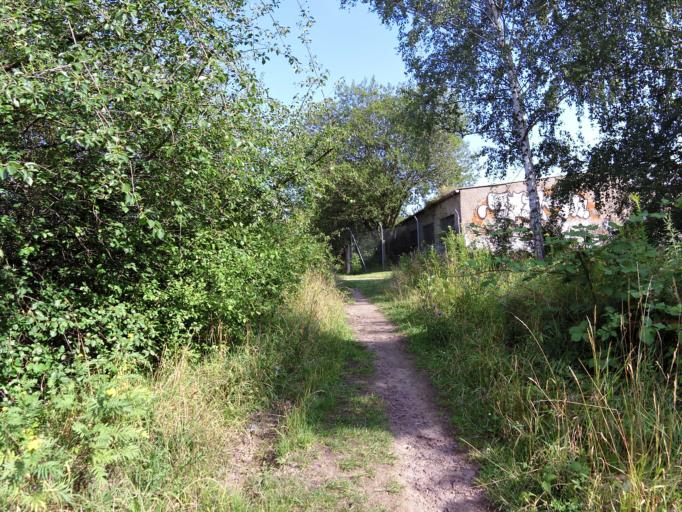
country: DE
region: Saxony
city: Leipzig
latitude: 51.3313
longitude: 12.3031
